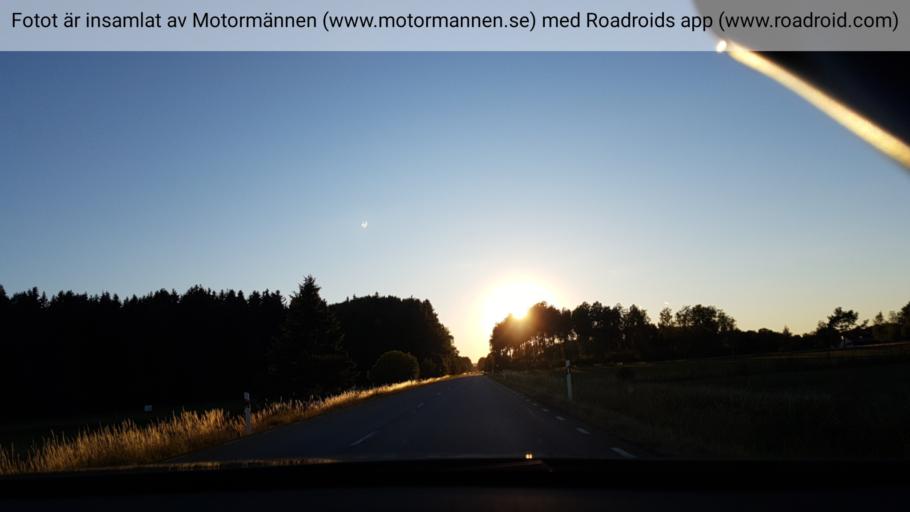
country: SE
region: Vaestra Goetaland
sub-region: Tidaholms Kommun
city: Olofstorp
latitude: 58.3638
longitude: 14.0250
